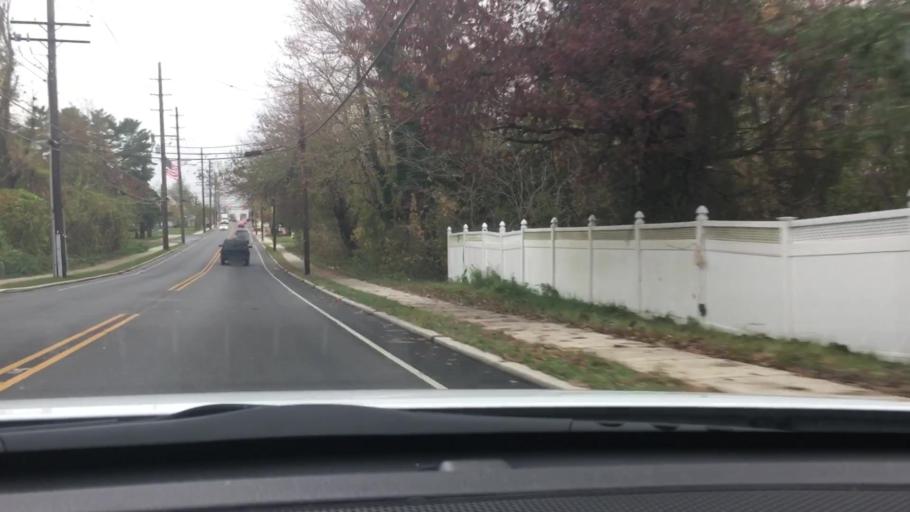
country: US
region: New Jersey
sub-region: Atlantic County
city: Pleasantville
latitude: 39.4061
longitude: -74.5160
